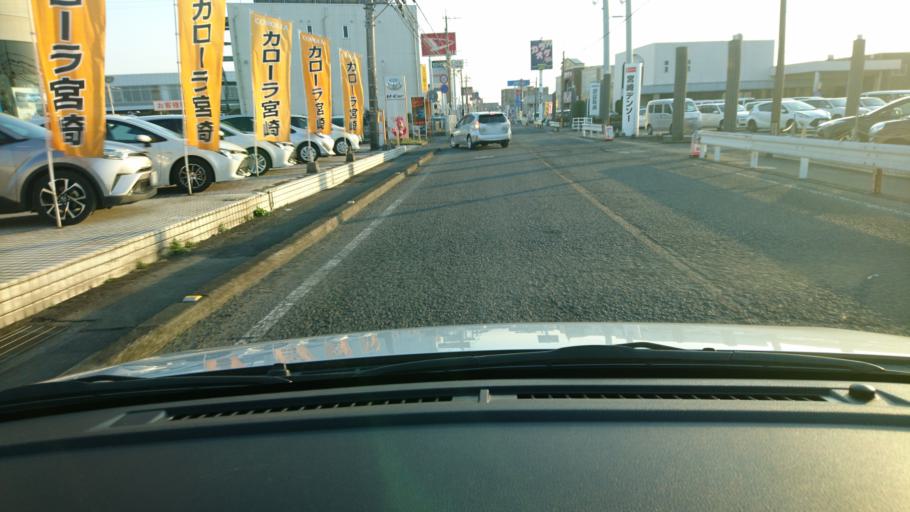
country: JP
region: Miyazaki
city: Miyazaki-shi
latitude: 31.9545
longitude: 131.4350
